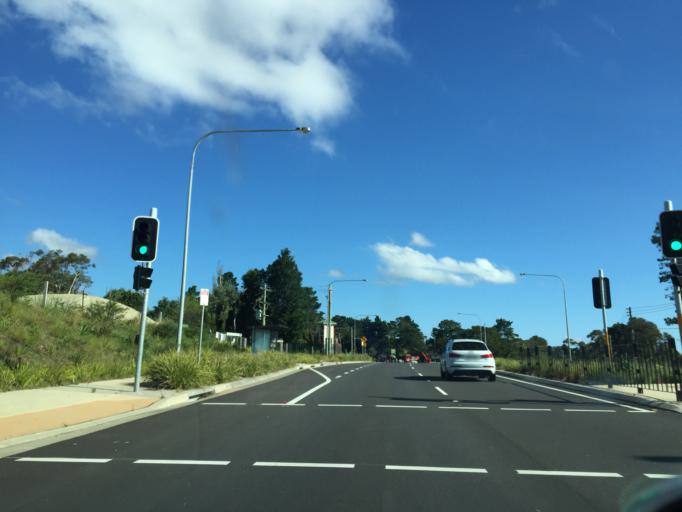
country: AU
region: New South Wales
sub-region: Blue Mountains Municipality
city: Lawson
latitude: -33.7230
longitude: 150.3843
